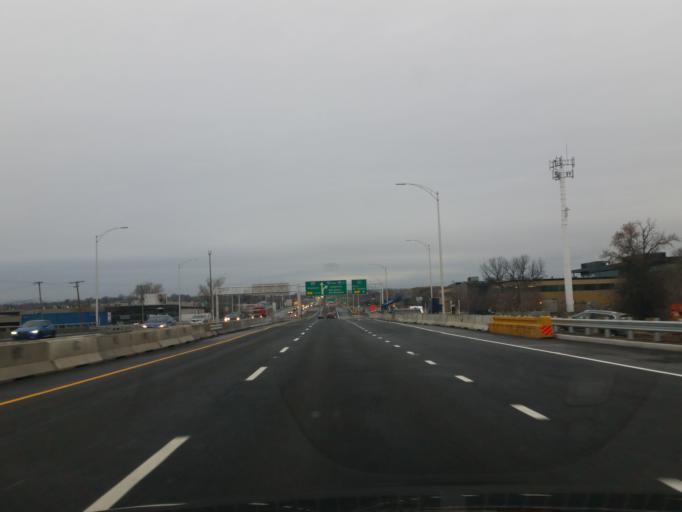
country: CA
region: Quebec
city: L'Ancienne-Lorette
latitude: 46.8004
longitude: -71.3236
